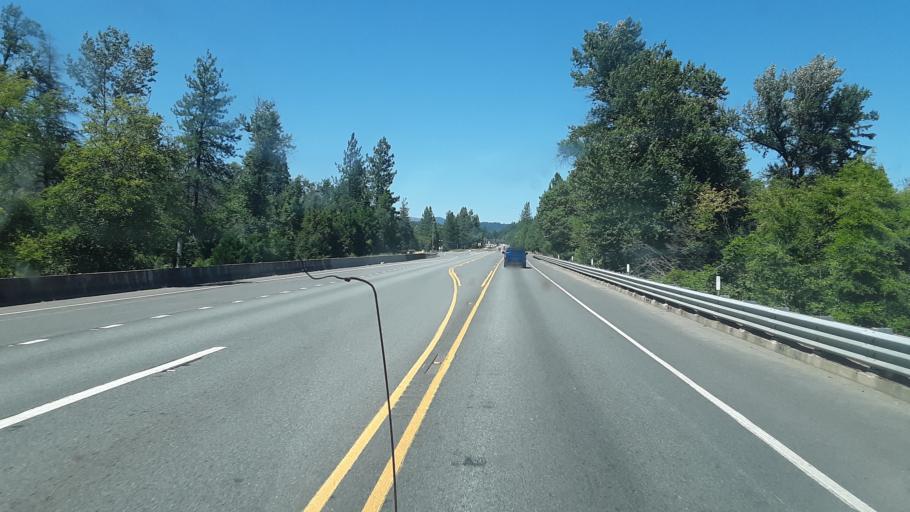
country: US
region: Oregon
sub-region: Josephine County
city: Cave Junction
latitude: 42.2708
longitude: -123.6192
